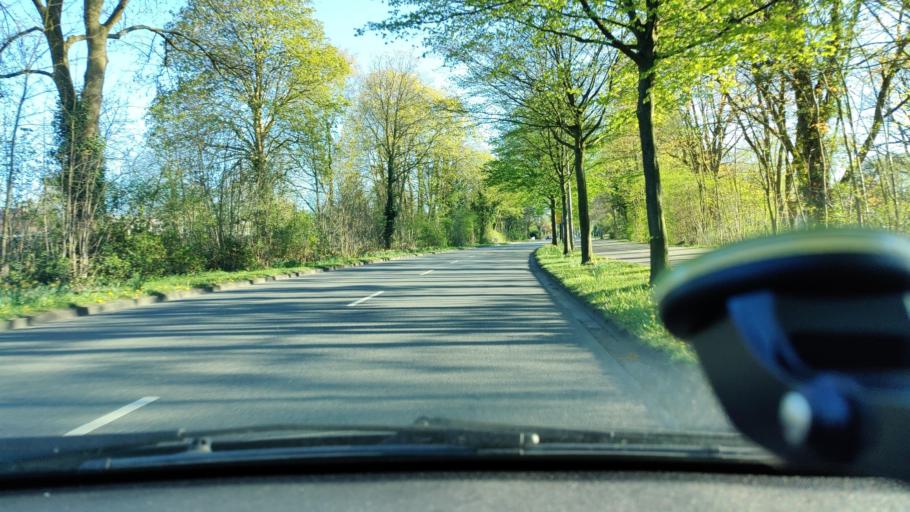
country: DE
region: North Rhine-Westphalia
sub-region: Regierungsbezirk Munster
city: Ahaus
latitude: 52.0810
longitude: 6.9984
